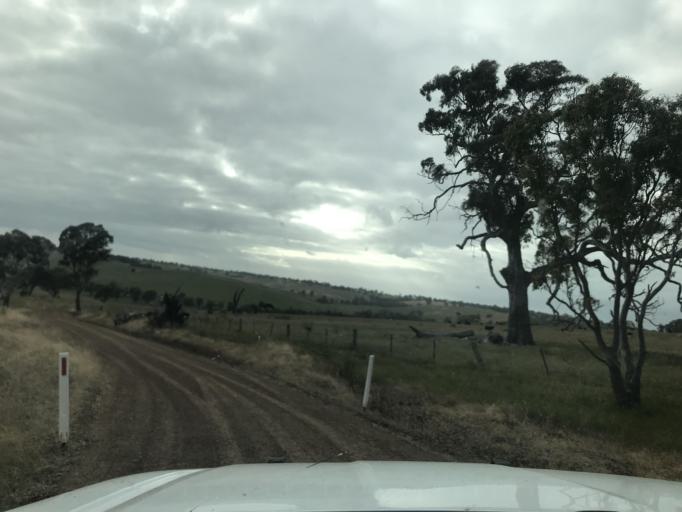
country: AU
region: South Australia
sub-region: Wattle Range
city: Penola
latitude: -37.2796
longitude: 141.3957
